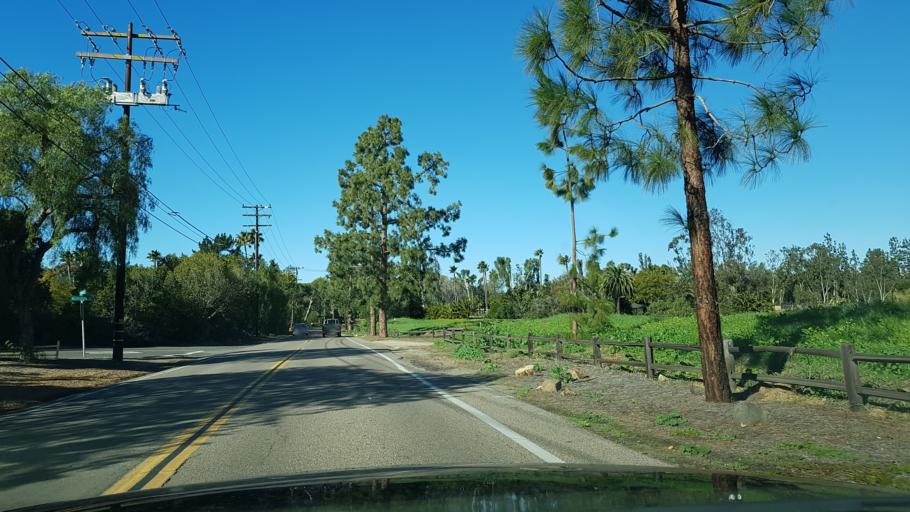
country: US
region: California
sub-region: San Diego County
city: Rancho Santa Fe
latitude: 33.0309
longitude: -117.1918
